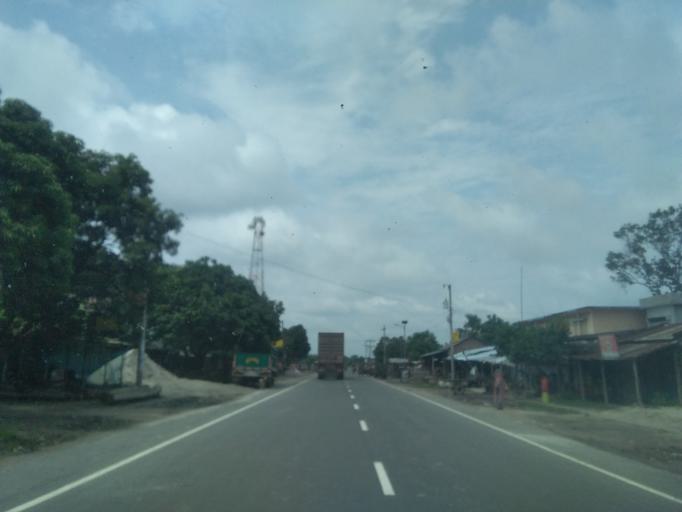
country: BD
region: Khulna
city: Kesabpur
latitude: 22.8125
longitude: 89.2455
